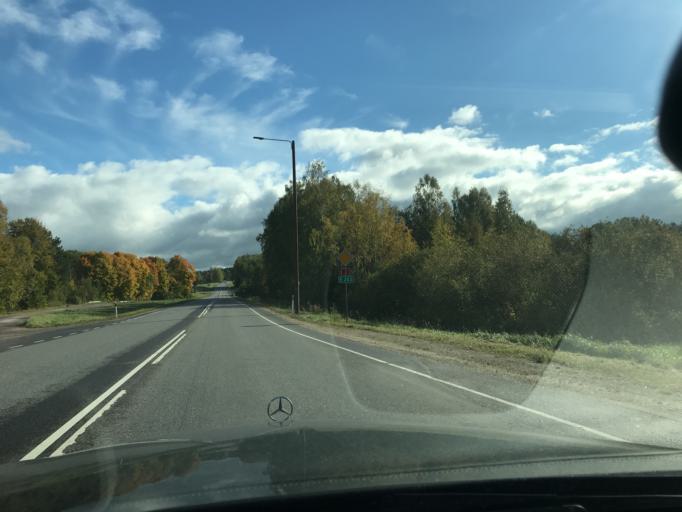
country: EE
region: Vorumaa
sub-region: Voru linn
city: Voru
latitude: 57.8088
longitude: 27.0675
